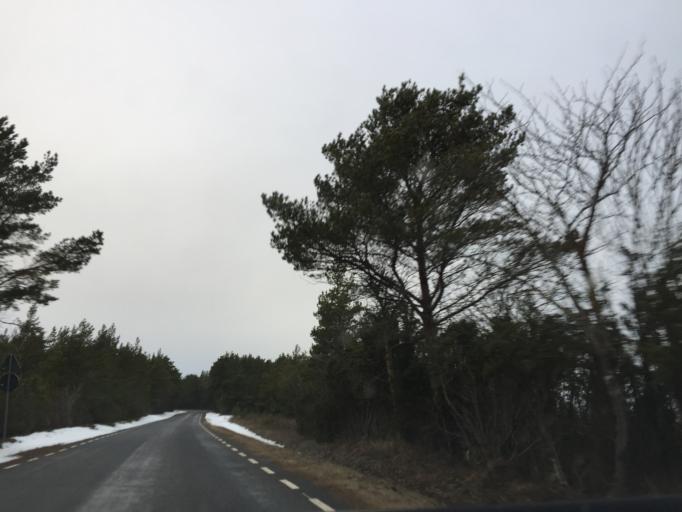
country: EE
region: Saare
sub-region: Kuressaare linn
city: Kuressaare
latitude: 58.5681
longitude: 22.3003
